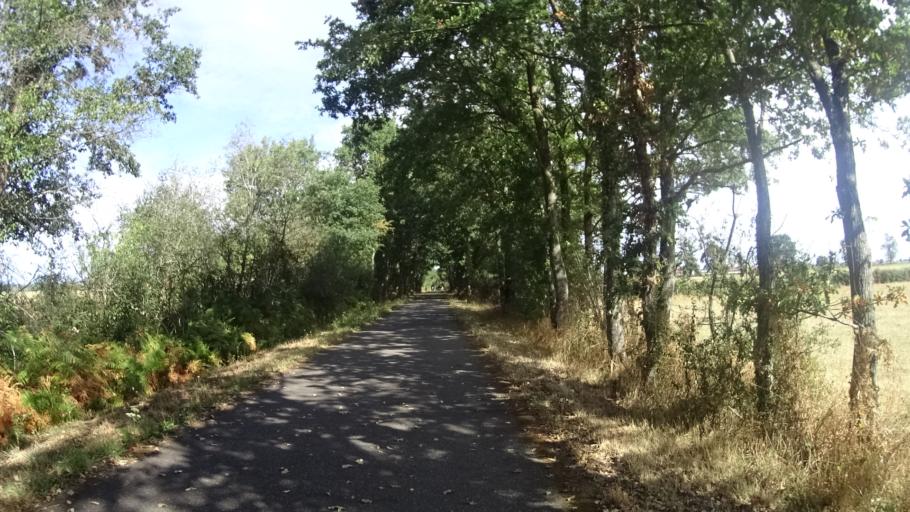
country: FR
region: Bourgogne
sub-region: Departement de Saone-et-Loire
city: Bourbon-Lancy
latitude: 46.6144
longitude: 3.7422
